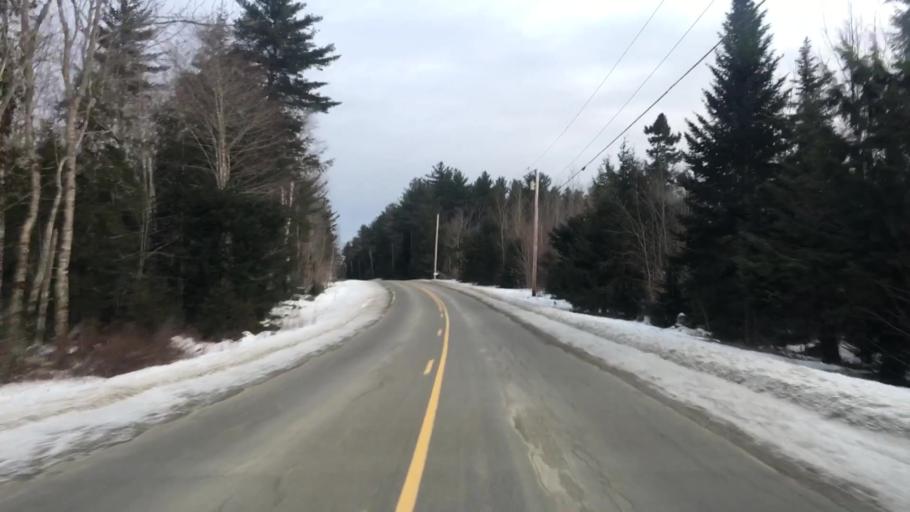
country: US
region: Maine
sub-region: Hancock County
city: Franklin
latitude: 44.7625
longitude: -68.3249
